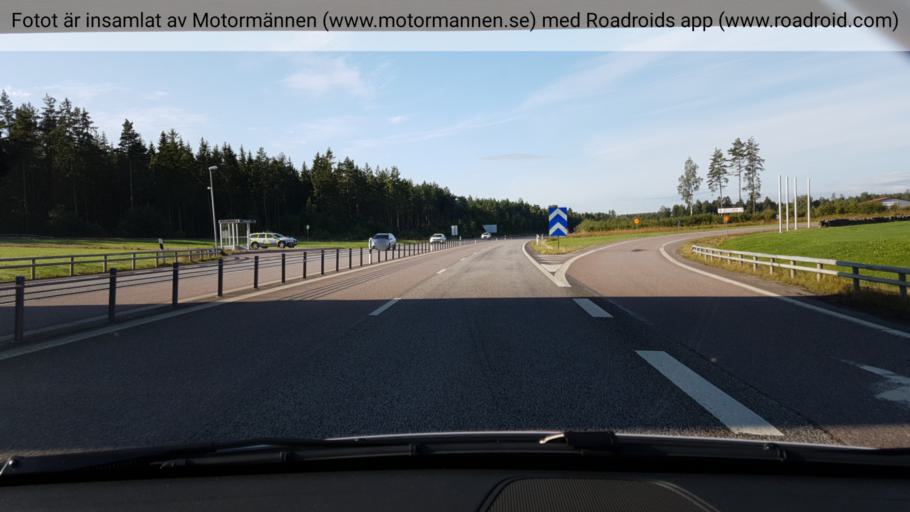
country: SE
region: Vaestra Goetaland
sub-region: Skovde Kommun
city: Skultorp
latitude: 58.3407
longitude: 13.8642
